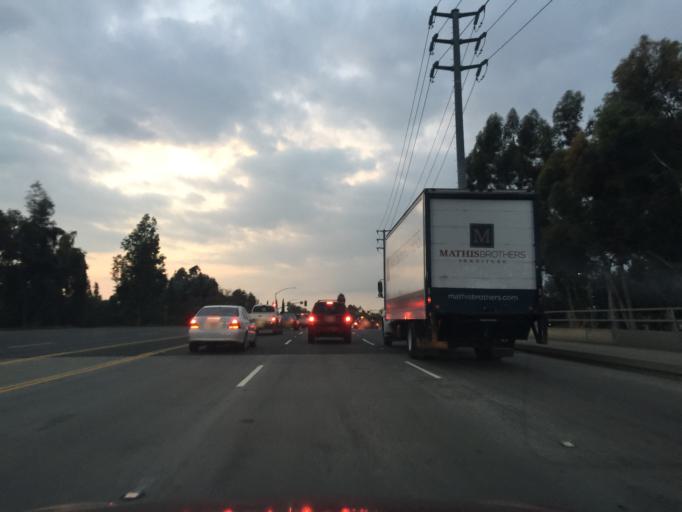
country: US
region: California
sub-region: Orange County
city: Brea
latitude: 33.9109
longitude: -117.8837
